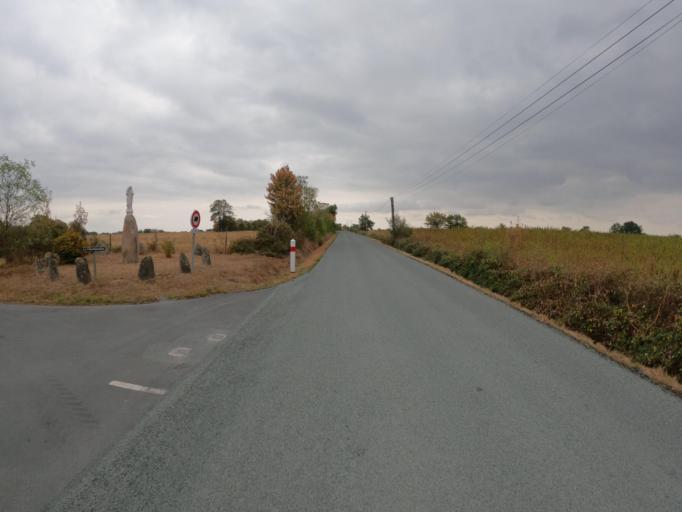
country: FR
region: Pays de la Loire
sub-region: Departement de la Vendee
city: Treize-Septiers
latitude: 46.9810
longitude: -1.2185
